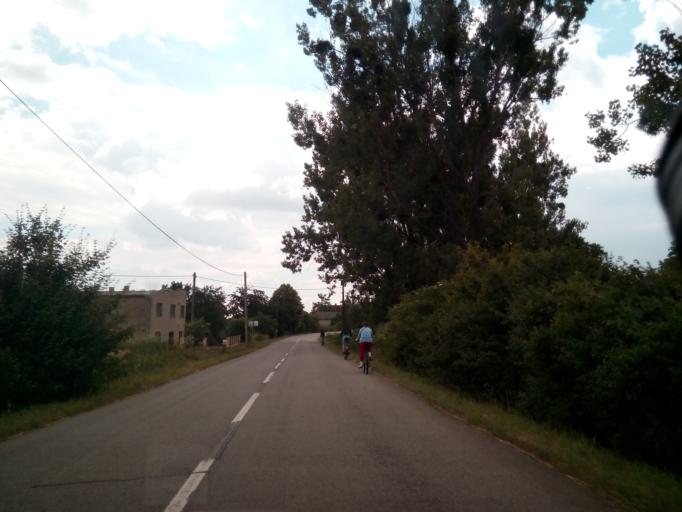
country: SK
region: Kosicky
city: Secovce
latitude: 48.5892
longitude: 21.5653
